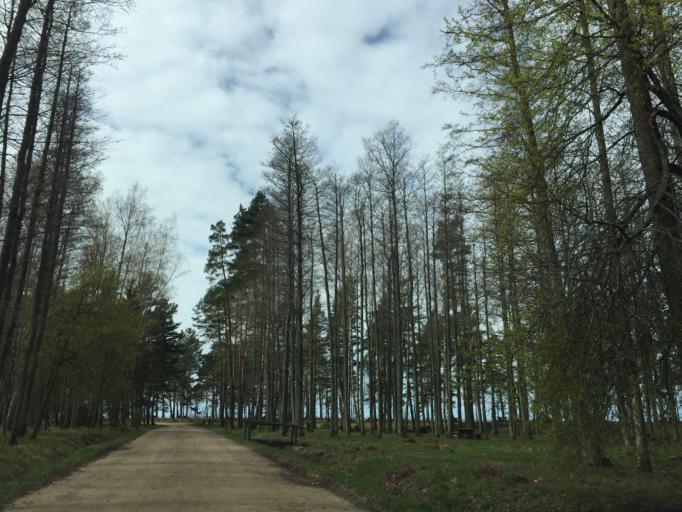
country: LV
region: Salacgrivas
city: Salacgriva
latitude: 57.5817
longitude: 24.3674
